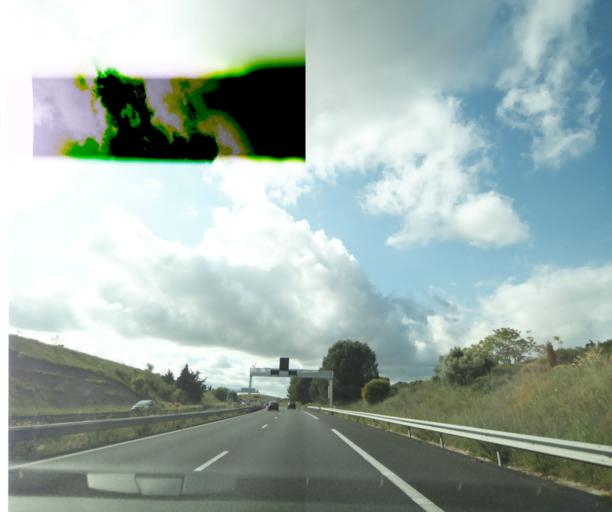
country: FR
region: Languedoc-Roussillon
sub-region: Departement du Gard
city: Garons
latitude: 43.7808
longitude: 4.4127
